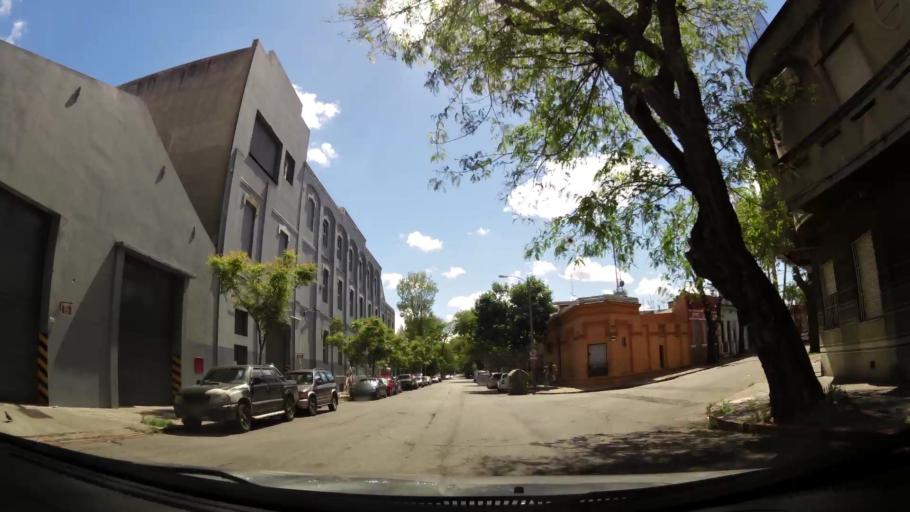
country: UY
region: Montevideo
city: Montevideo
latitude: -34.8843
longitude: -56.1920
